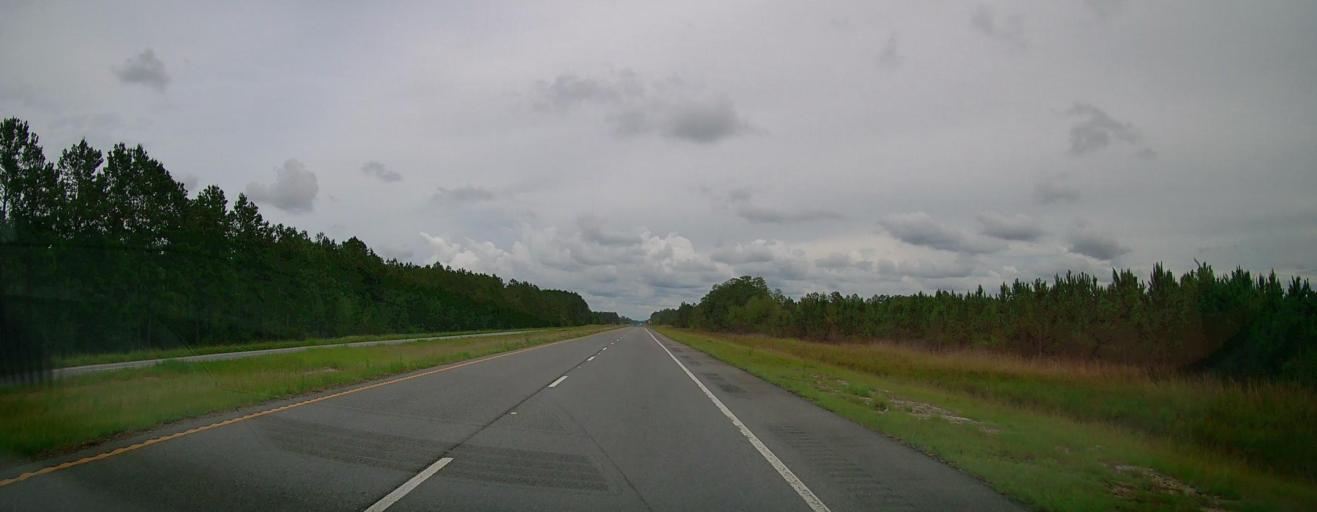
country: US
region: Georgia
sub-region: Appling County
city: Baxley
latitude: 31.7467
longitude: -82.2571
